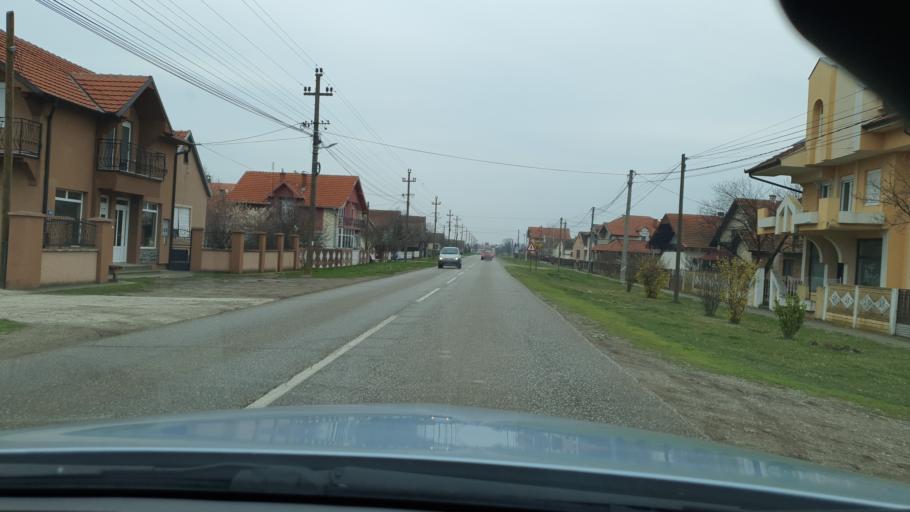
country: RS
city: Belotic
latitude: 44.8158
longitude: 19.5324
